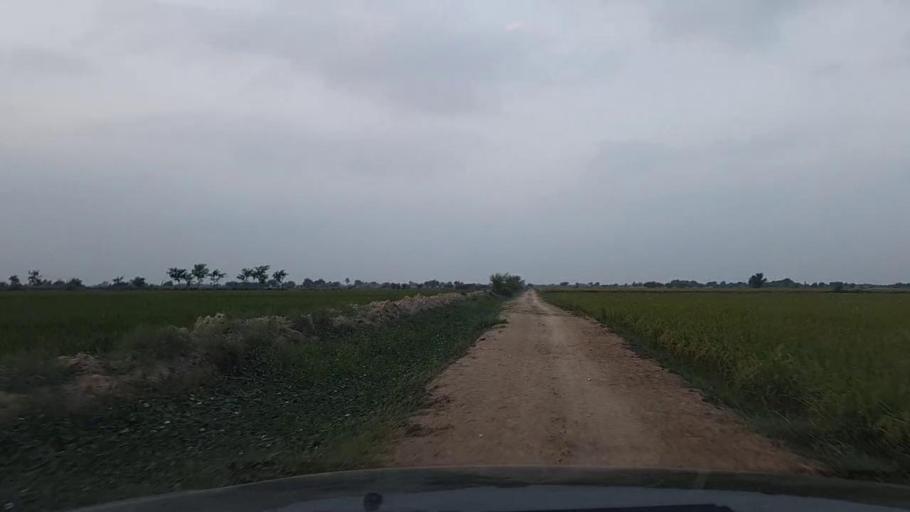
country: PK
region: Sindh
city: Jati
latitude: 24.5050
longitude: 68.3931
